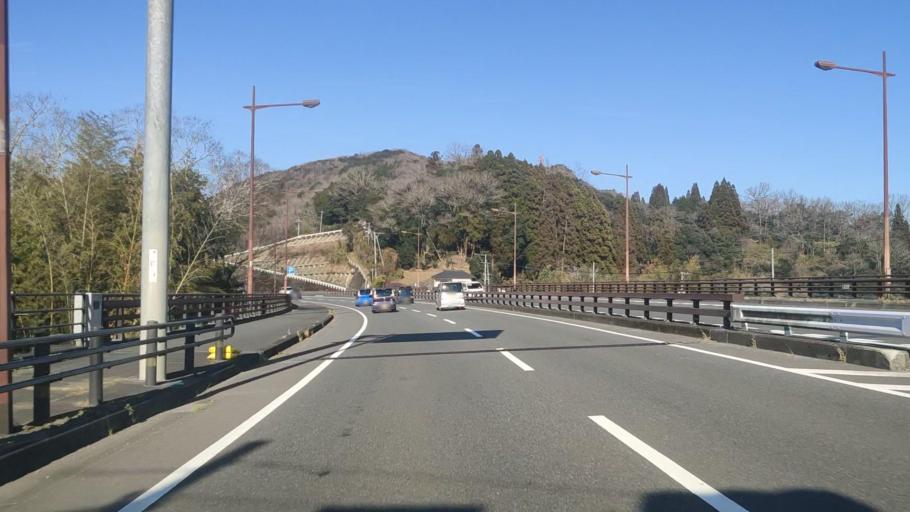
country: JP
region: Oita
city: Oita
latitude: 33.1090
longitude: 131.6564
